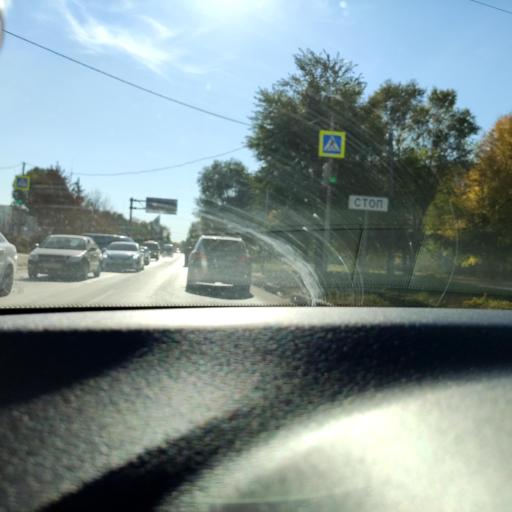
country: RU
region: Samara
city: Petra-Dubrava
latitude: 53.2484
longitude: 50.2685
